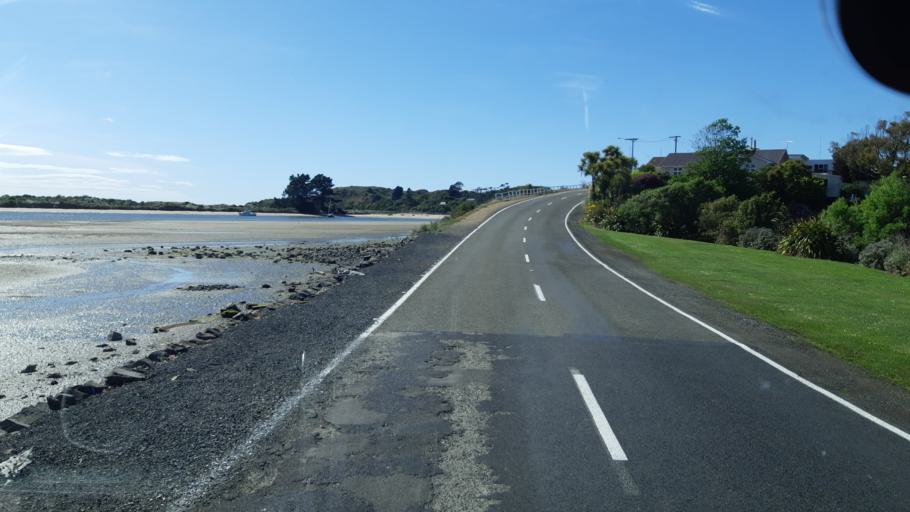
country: NZ
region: Otago
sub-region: Dunedin City
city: Portobello
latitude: -45.6374
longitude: 170.6552
